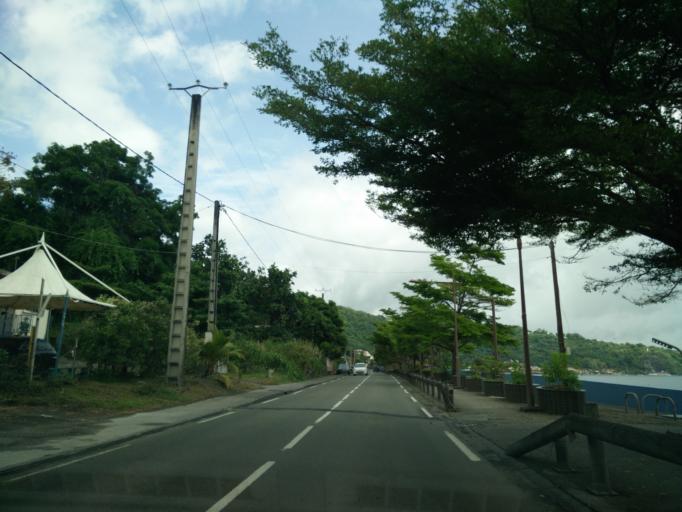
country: MQ
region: Martinique
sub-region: Martinique
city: Saint-Pierre
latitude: 14.7523
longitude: -61.1810
